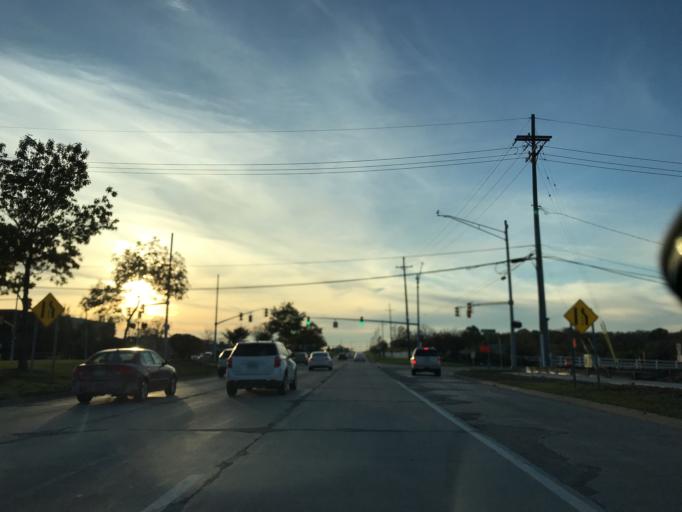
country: US
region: Michigan
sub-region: Oakland County
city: Novi
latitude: 42.4963
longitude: -83.4557
